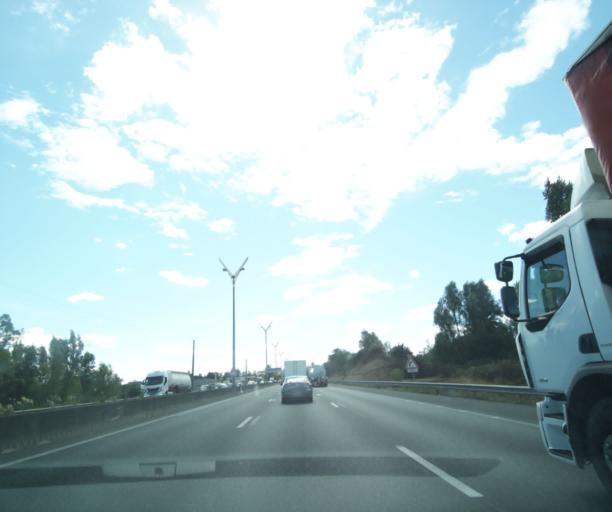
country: FR
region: Aquitaine
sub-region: Departement de la Gironde
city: Villenave-d'Ornon
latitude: 44.7867
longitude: -0.5415
